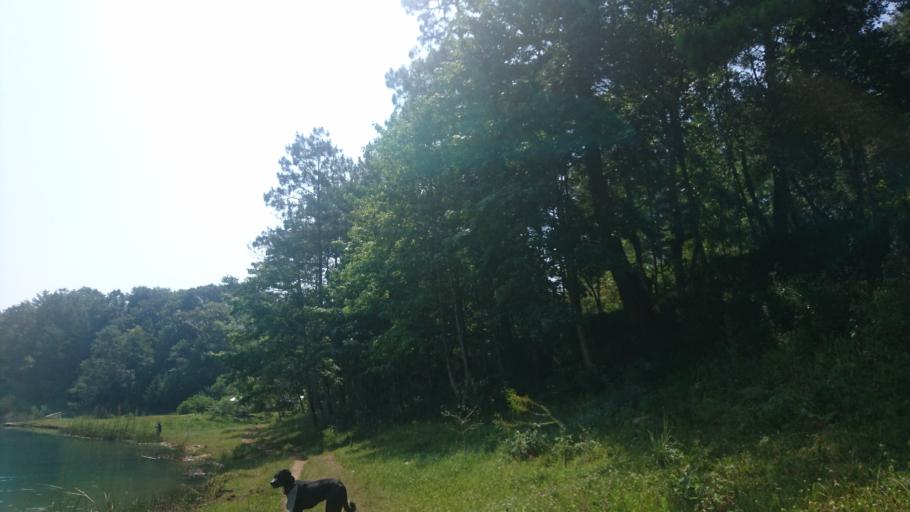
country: GT
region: Huehuetenango
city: Union
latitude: 16.0730
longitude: -91.6819
